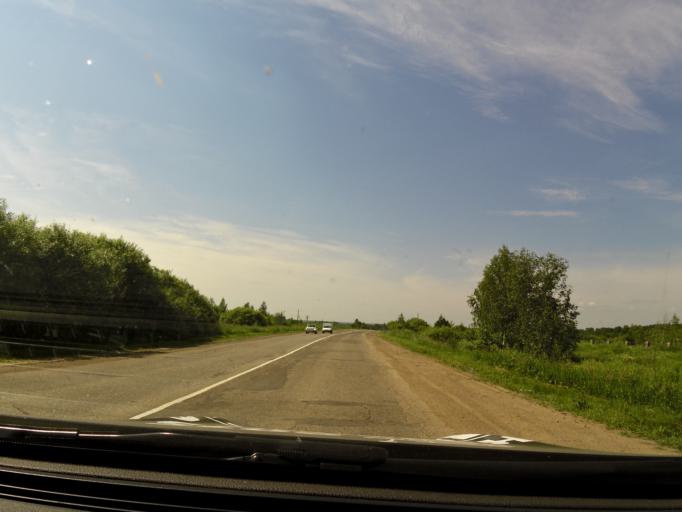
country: RU
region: Kostroma
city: Galich
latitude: 58.4438
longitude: 42.5211
